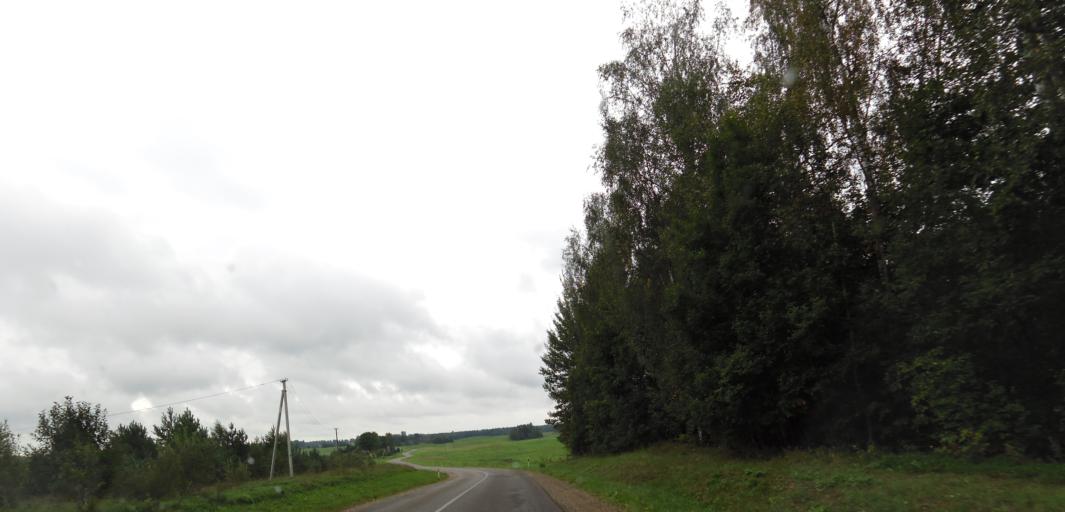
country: LT
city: Moletai
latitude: 55.3046
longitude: 25.3432
